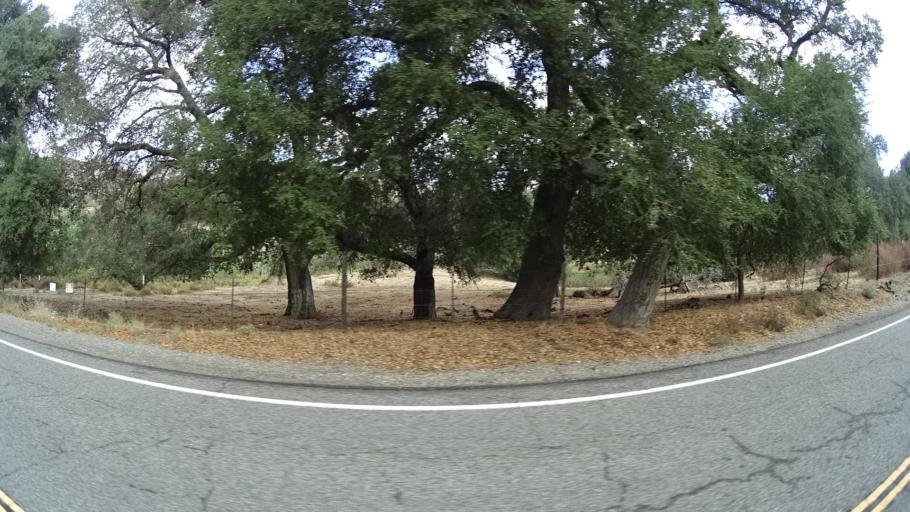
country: MX
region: Baja California
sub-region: Tecate
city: Hacienda Tecate
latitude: 32.5908
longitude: -116.5126
